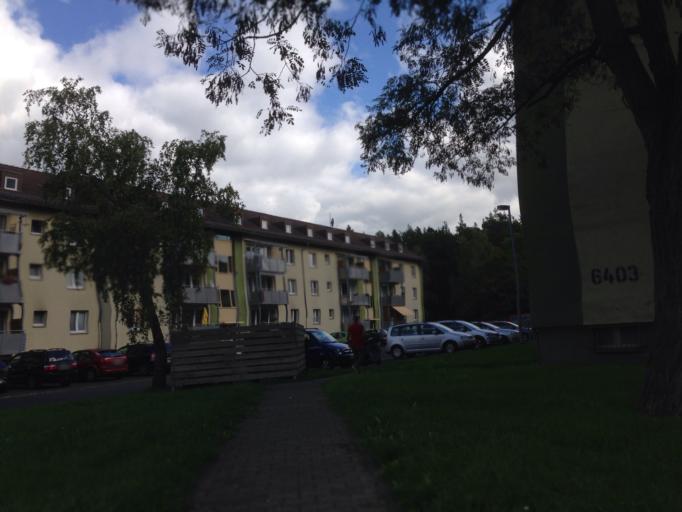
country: DE
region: Hesse
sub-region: Regierungsbezirk Giessen
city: Giessen
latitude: 50.5867
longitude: 8.7195
